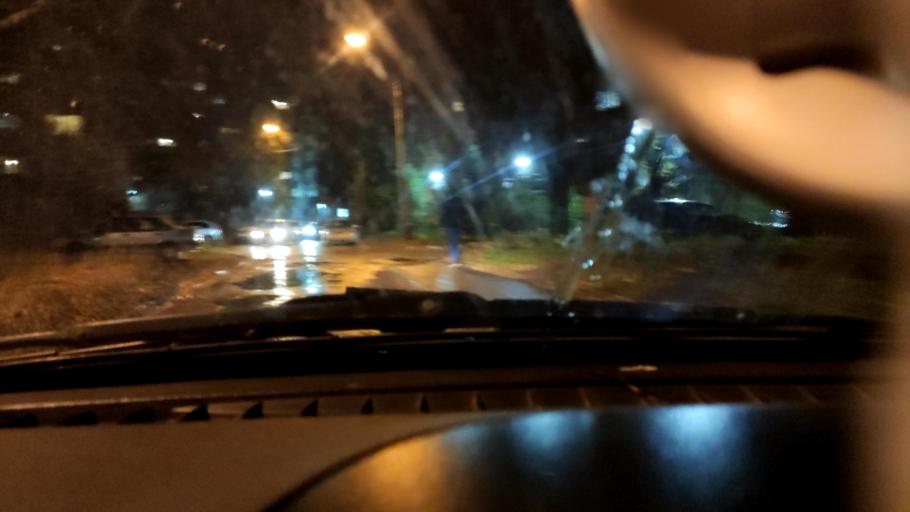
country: RU
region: Perm
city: Perm
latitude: 58.0213
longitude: 56.2695
